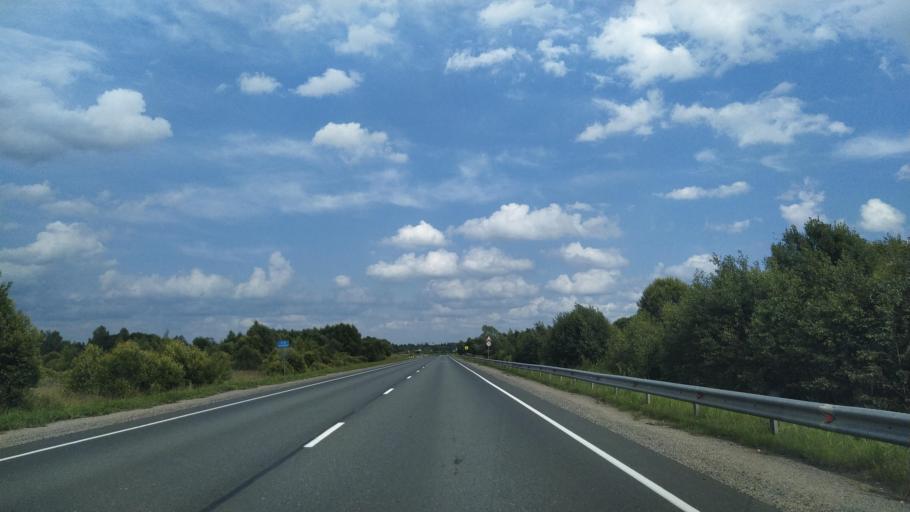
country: RU
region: Pskov
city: Dno
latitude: 57.9815
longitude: 29.7440
